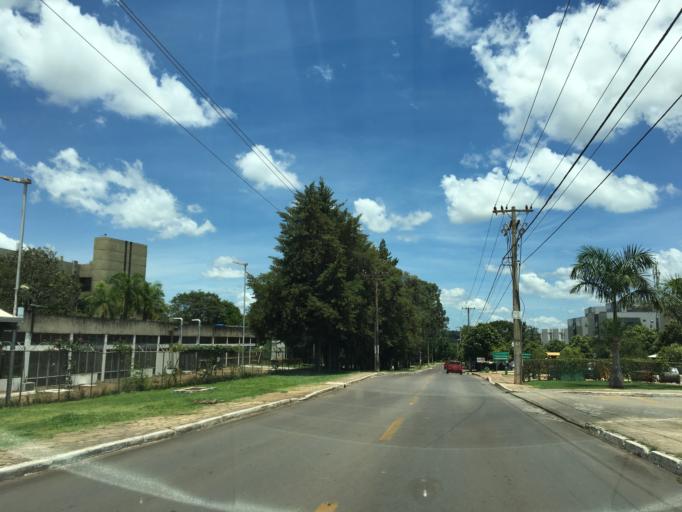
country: BR
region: Federal District
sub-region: Brasilia
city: Brasilia
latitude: -15.7323
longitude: -47.8985
